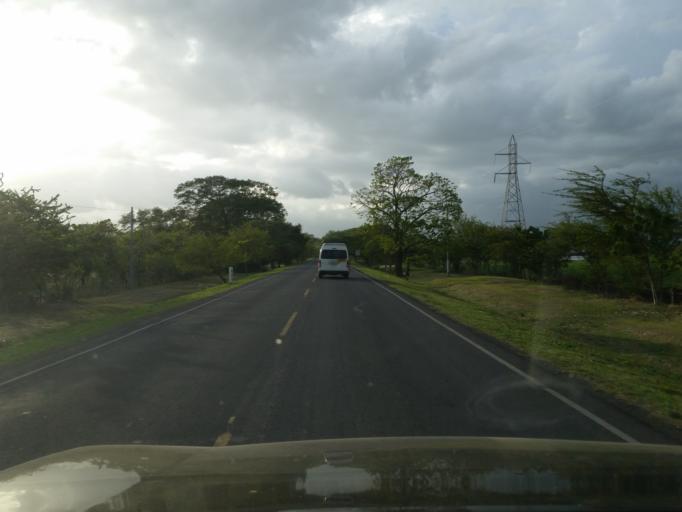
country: NI
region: Granada
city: Nandaime
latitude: 11.6831
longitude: -85.9876
